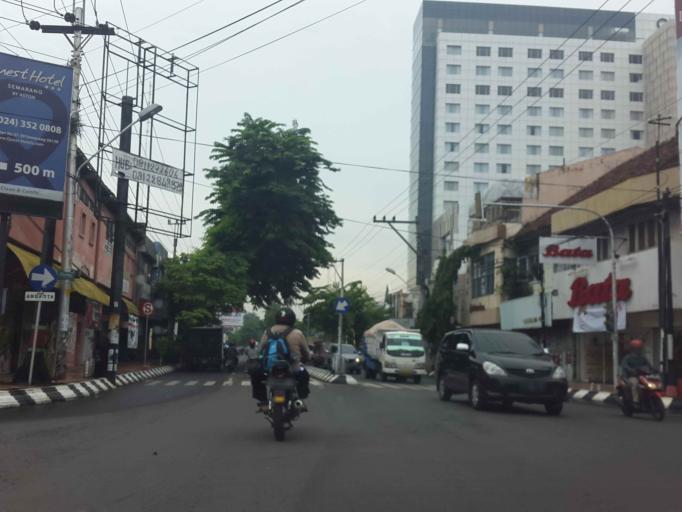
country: ID
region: Central Java
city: Semarang
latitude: -6.9764
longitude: 110.4205
